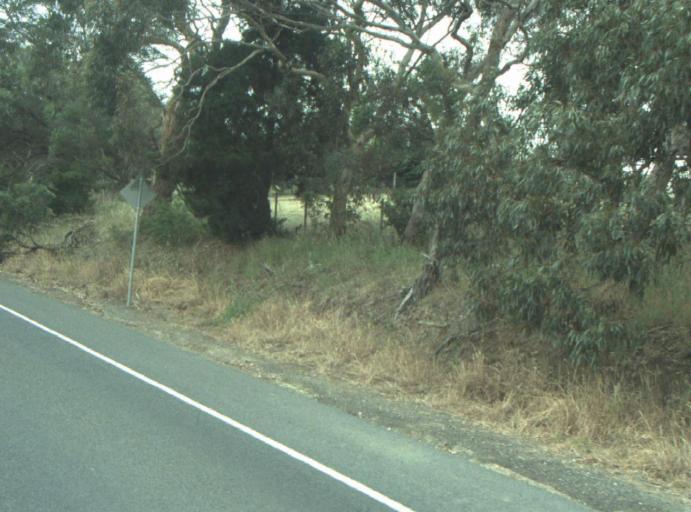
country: AU
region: Victoria
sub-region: Greater Geelong
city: Leopold
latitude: -38.2166
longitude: 144.5062
